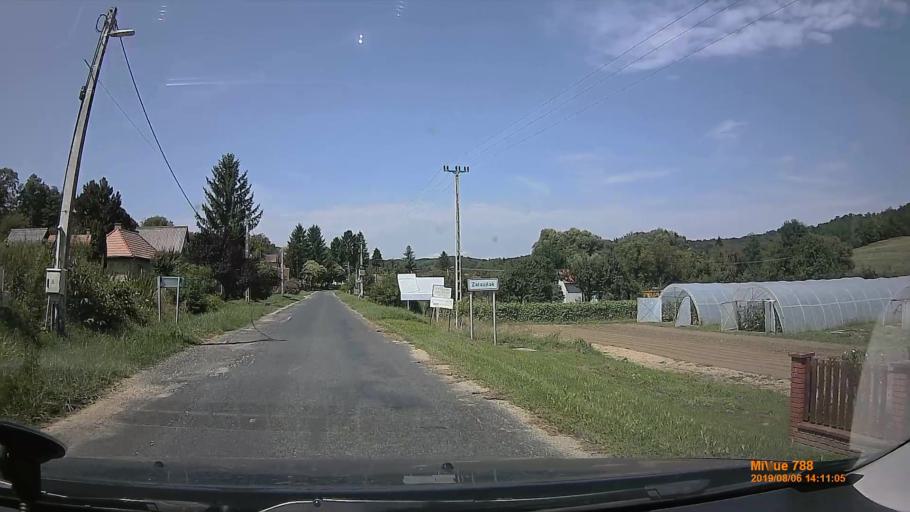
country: HU
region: Zala
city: Zalakomar
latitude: 46.5549
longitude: 17.0798
